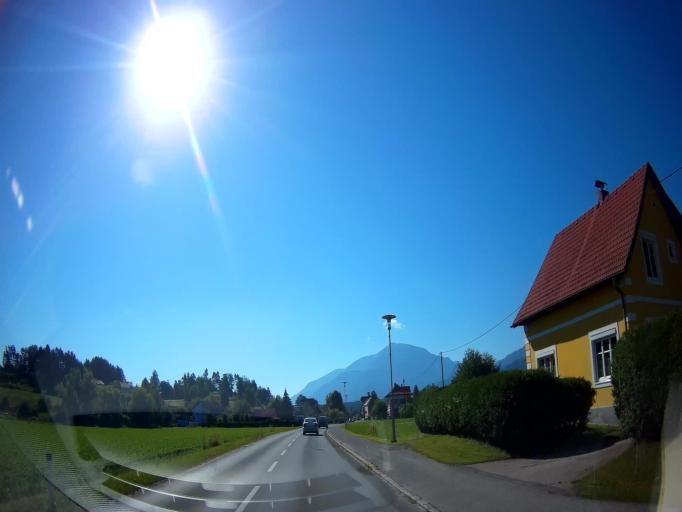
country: AT
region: Carinthia
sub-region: Politischer Bezirk Volkermarkt
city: Eberndorf
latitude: 46.5895
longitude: 14.6438
